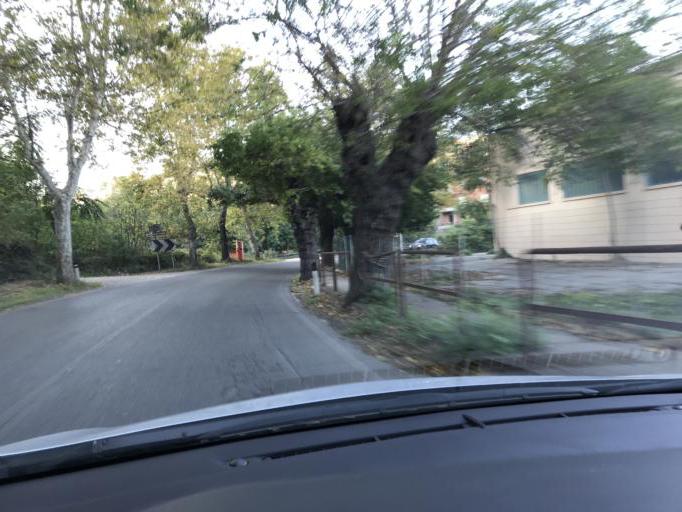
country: IT
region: Latium
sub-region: Provincia di Viterbo
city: Orte
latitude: 42.4553
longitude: 12.3867
